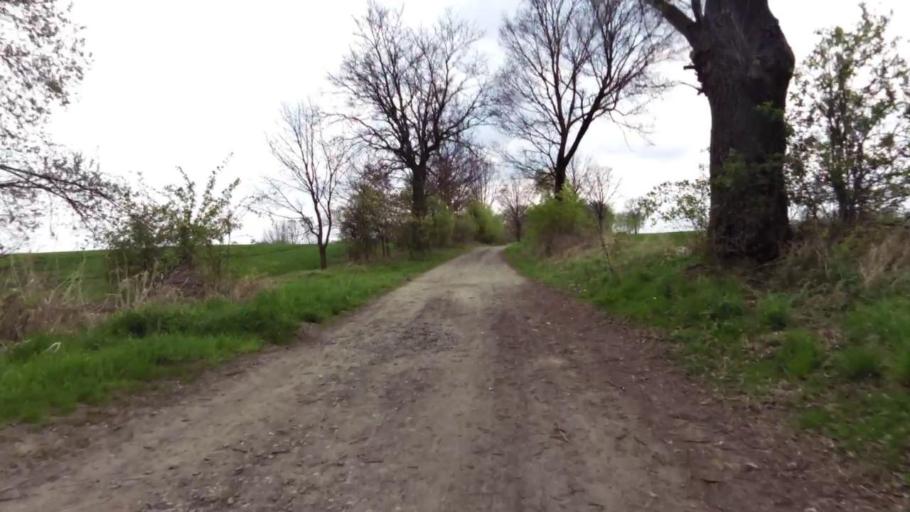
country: PL
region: West Pomeranian Voivodeship
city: Trzcinsko Zdroj
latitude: 52.9469
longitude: 14.6635
